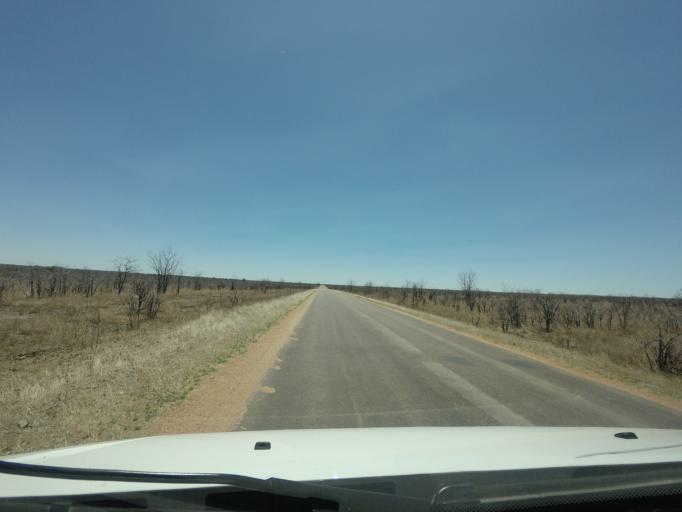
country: ZA
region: Limpopo
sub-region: Mopani District Municipality
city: Phalaborwa
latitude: -23.5804
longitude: 31.4504
